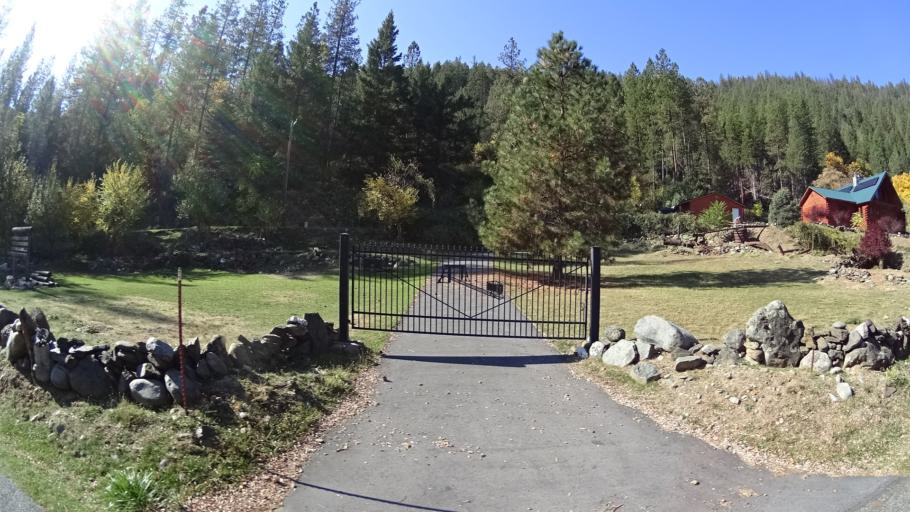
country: US
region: California
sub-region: Siskiyou County
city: Yreka
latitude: 41.7471
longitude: -123.0087
